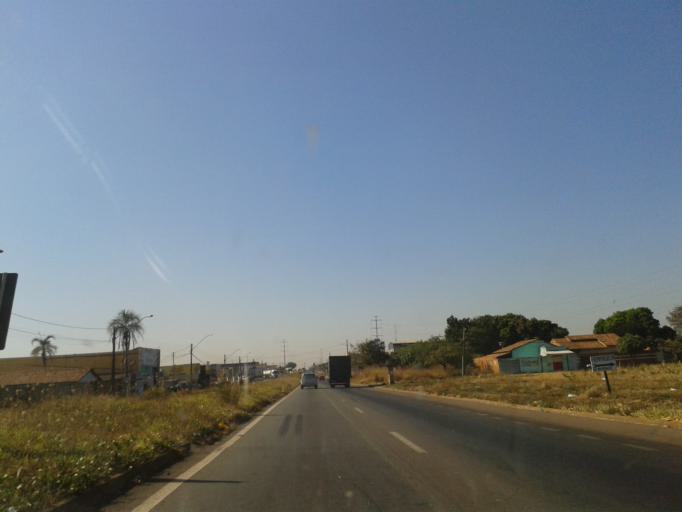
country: BR
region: Goias
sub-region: Aparecida De Goiania
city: Aparecida de Goiania
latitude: -16.7741
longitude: -49.3034
